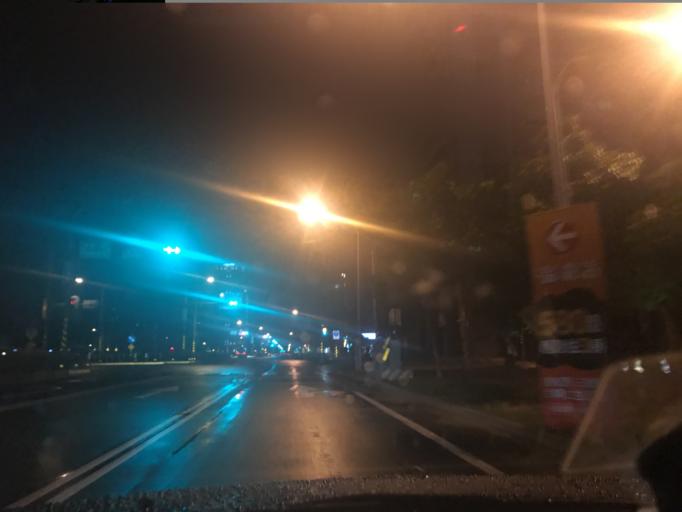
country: TW
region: Taiwan
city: Daxi
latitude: 24.9324
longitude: 121.2809
